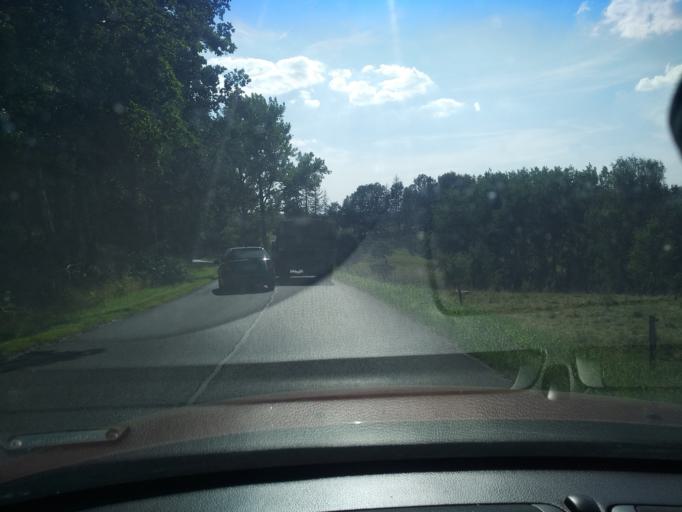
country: PL
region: Lower Silesian Voivodeship
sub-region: Powiat lubanski
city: Lesna
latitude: 51.0267
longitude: 15.2921
